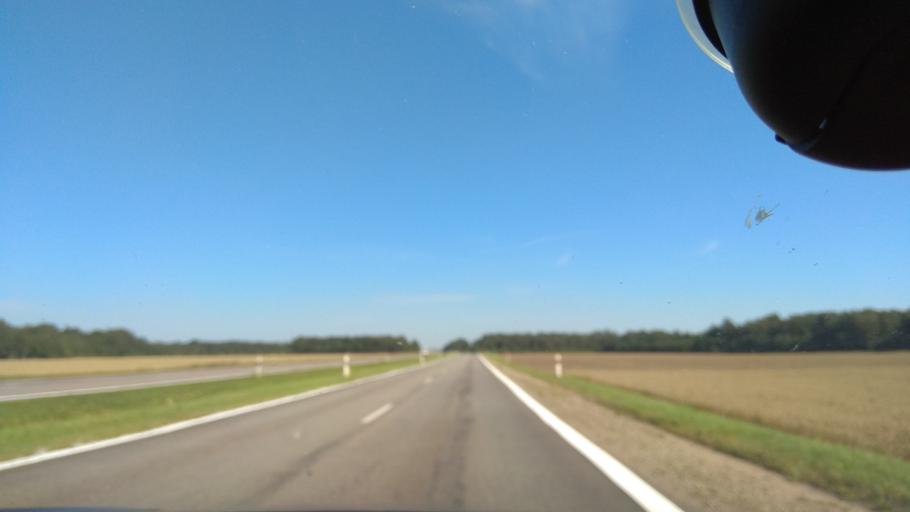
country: LT
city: Kursenai
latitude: 55.9917
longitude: 23.0391
